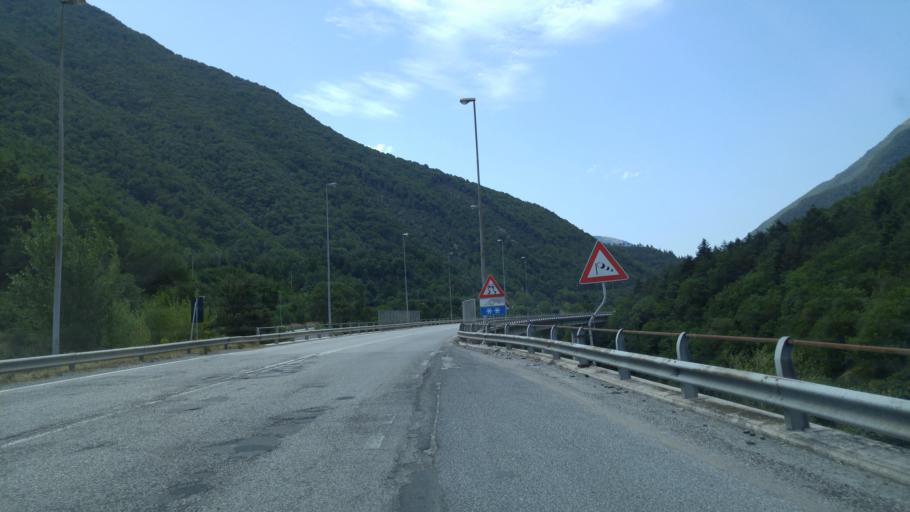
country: IT
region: The Marches
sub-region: Provincia di Pesaro e Urbino
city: Cagli
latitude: 43.5352
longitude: 12.6467
